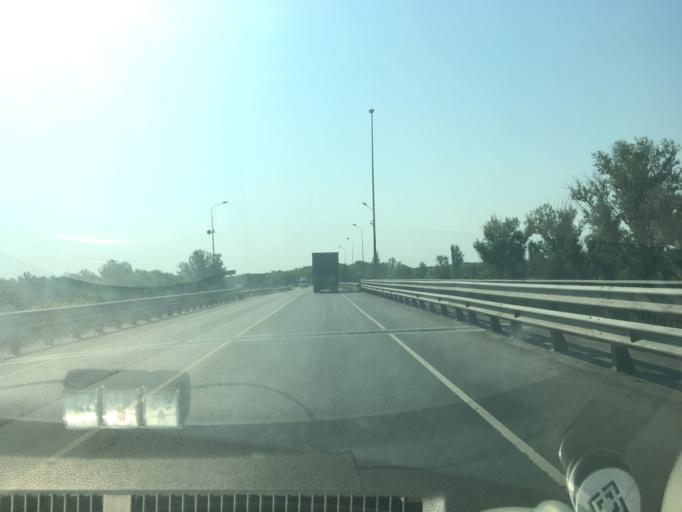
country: RU
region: Nizjnij Novgorod
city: Kstovo
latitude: 56.0977
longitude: 44.3100
